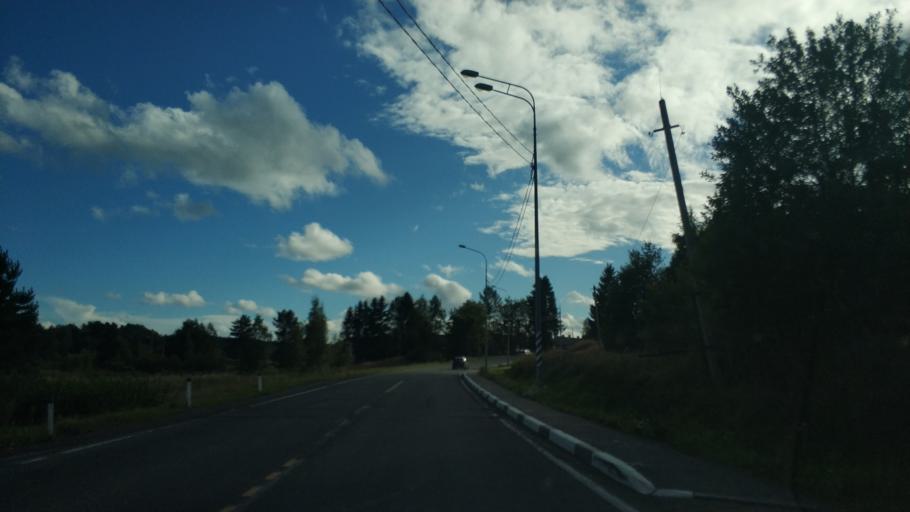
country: RU
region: Republic of Karelia
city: Lakhdenpokh'ya
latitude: 61.5539
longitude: 30.3218
